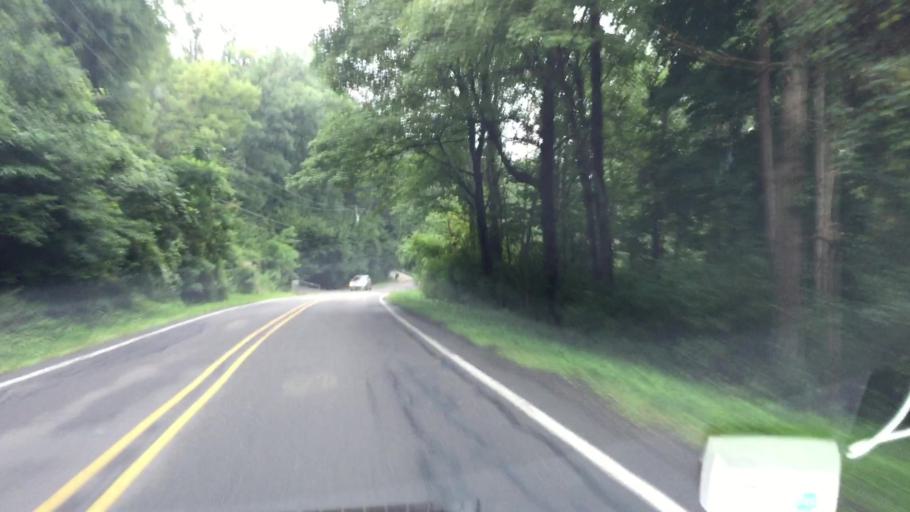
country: US
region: Pennsylvania
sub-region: Allegheny County
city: Bradford Woods
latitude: 40.6145
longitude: -80.0773
